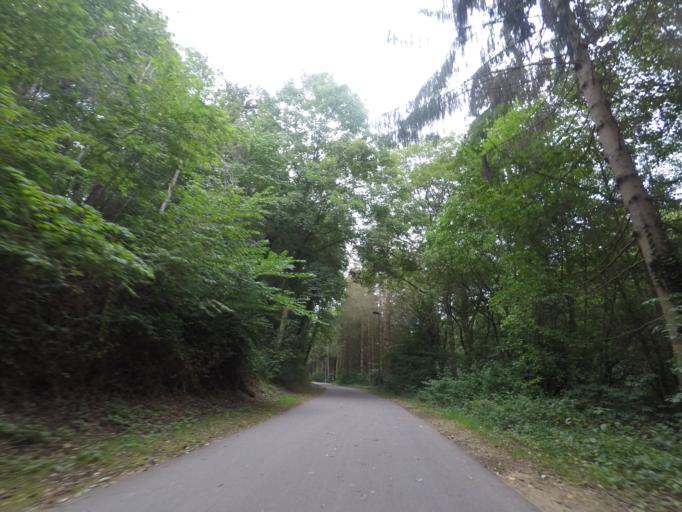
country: LU
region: Luxembourg
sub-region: Canton de Luxembourg
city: Luxembourg
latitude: 49.6008
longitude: 6.1480
